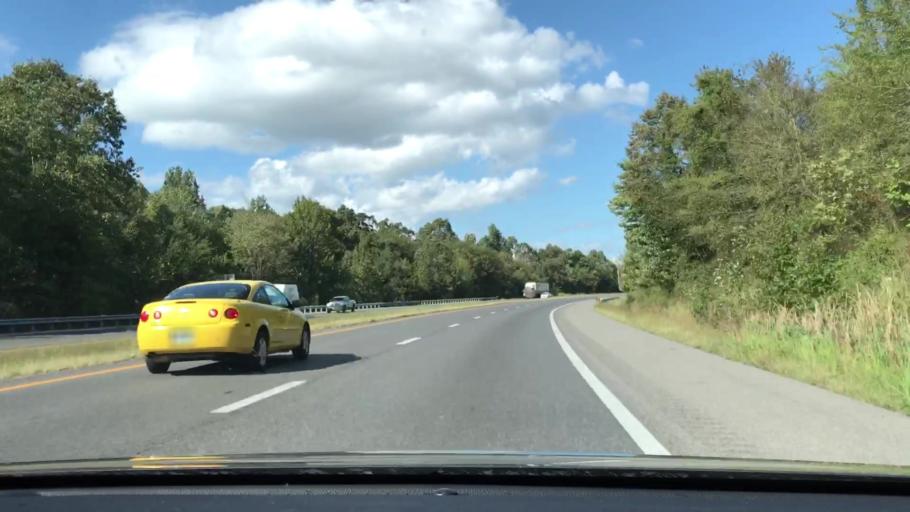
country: US
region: Kentucky
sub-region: Marshall County
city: Benton
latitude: 36.9189
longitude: -88.3513
